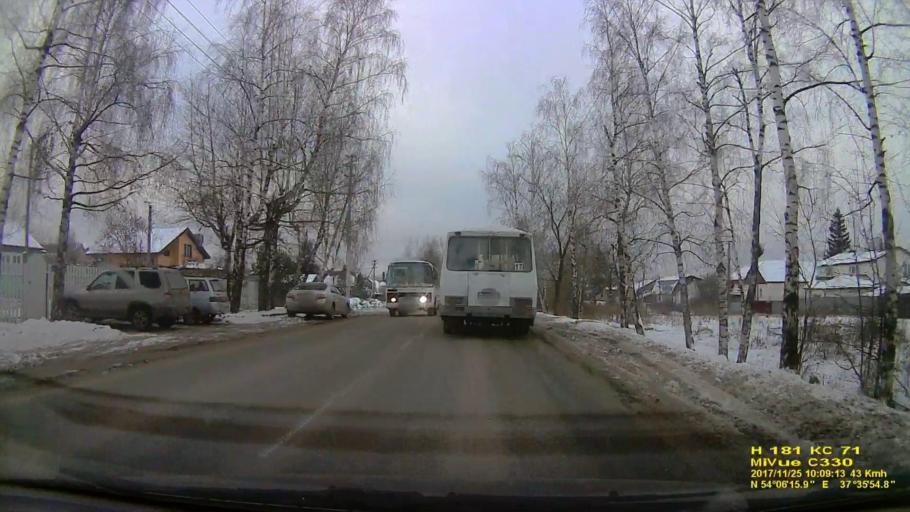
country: RU
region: Tula
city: Skuratovskiy
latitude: 54.1043
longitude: 37.5984
